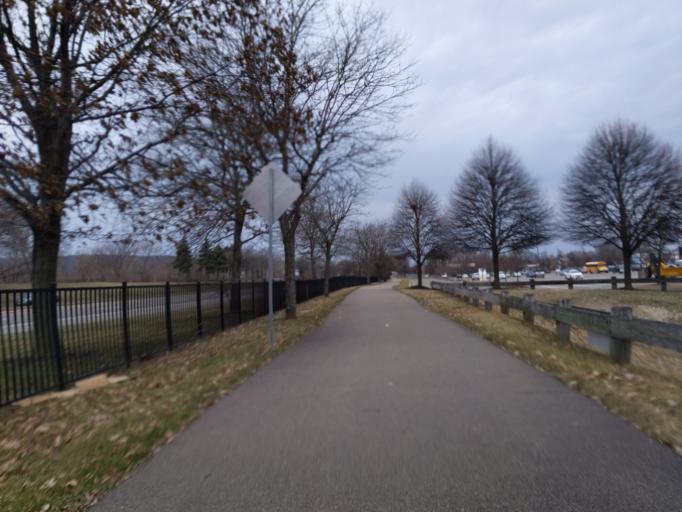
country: US
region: New York
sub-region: Chemung County
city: Elmira
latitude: 42.1037
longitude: -76.8096
